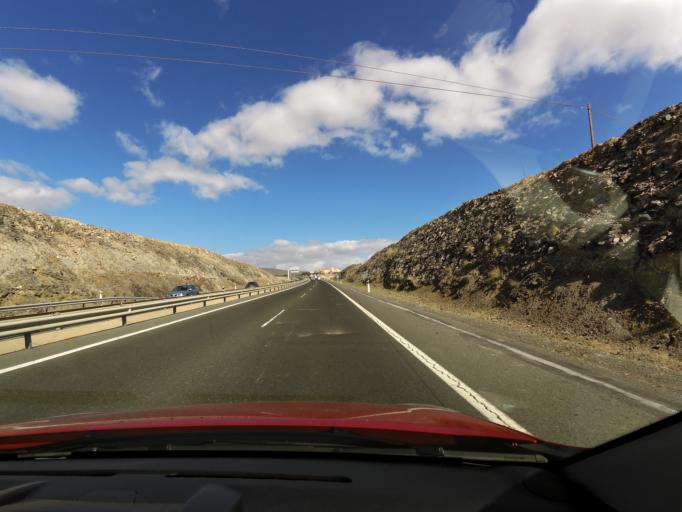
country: ES
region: Canary Islands
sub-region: Provincia de Las Palmas
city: Maspalomas
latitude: 27.7601
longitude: -15.6088
